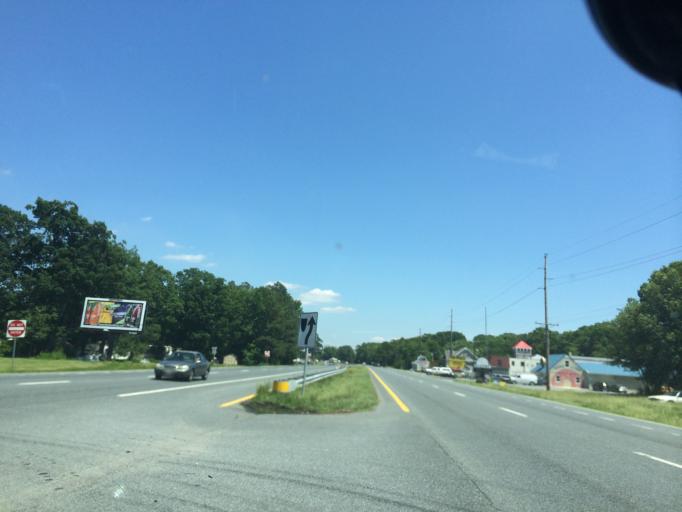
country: US
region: Maryland
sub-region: Dorchester County
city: Cambridge
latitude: 38.5516
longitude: -76.0347
